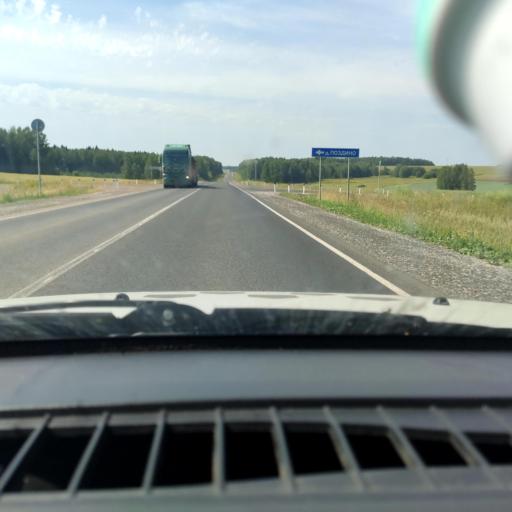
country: RU
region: Perm
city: Siva
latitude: 58.3959
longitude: 54.5162
